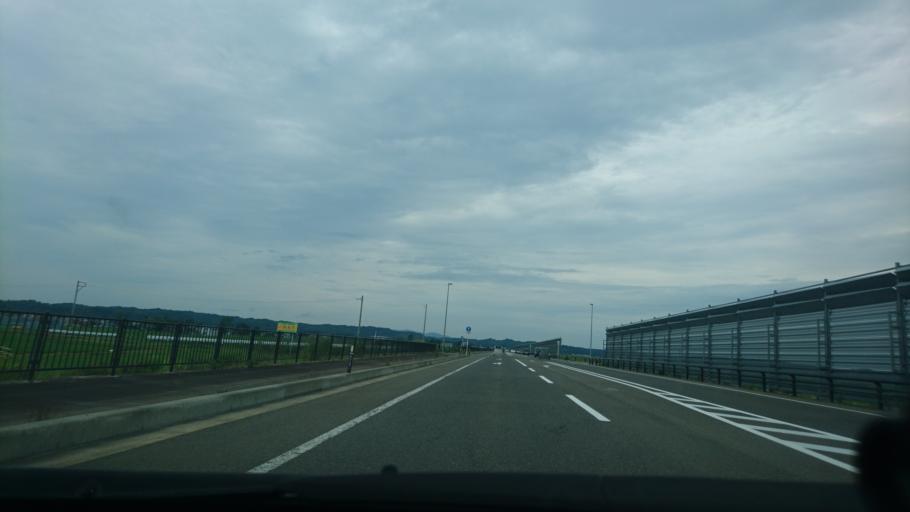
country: JP
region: Akita
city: Omagari
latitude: 39.5040
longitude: 140.4039
